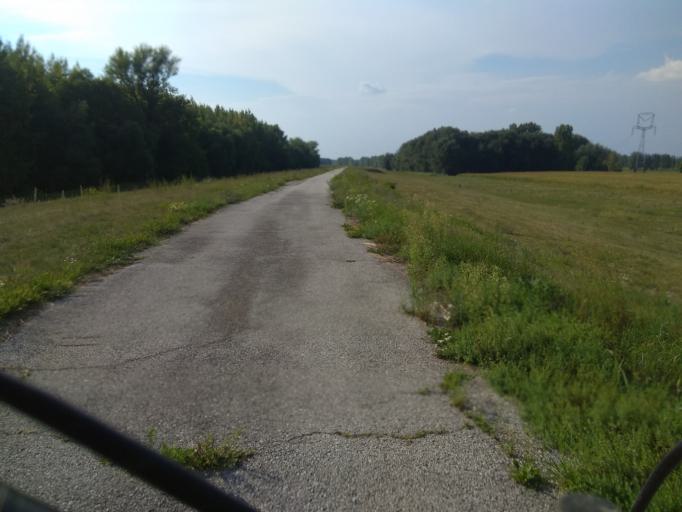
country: SK
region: Trnavsky
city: Gabcikovo
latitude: 47.8000
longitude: 17.6508
